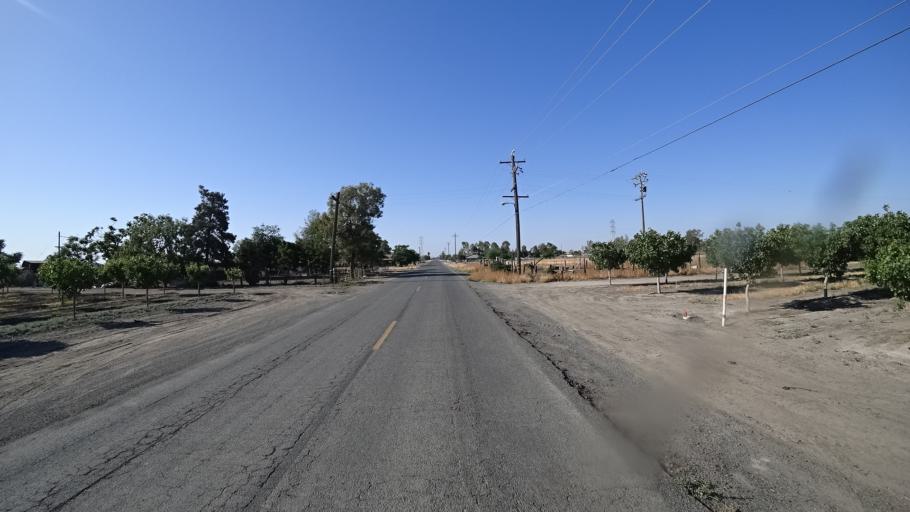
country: US
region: California
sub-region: Kings County
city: Corcoran
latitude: 36.1238
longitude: -119.5634
